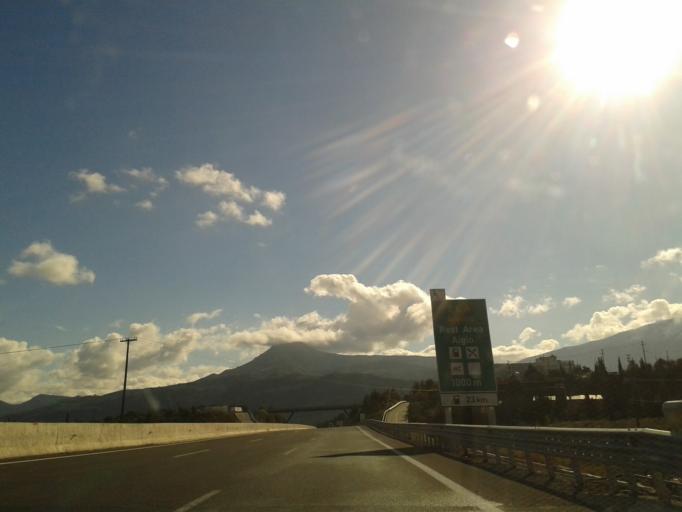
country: GR
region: West Greece
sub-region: Nomos Achaias
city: Aigio
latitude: 38.2457
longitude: 22.0727
